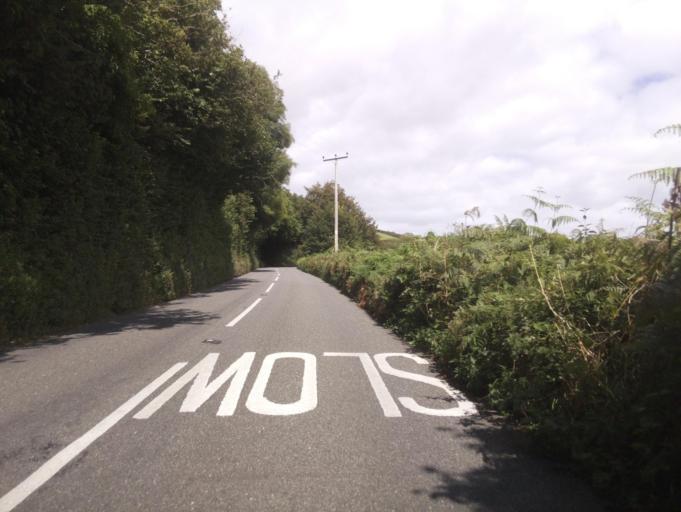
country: GB
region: England
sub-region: Devon
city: Dartmouth
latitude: 50.3626
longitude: -3.5610
